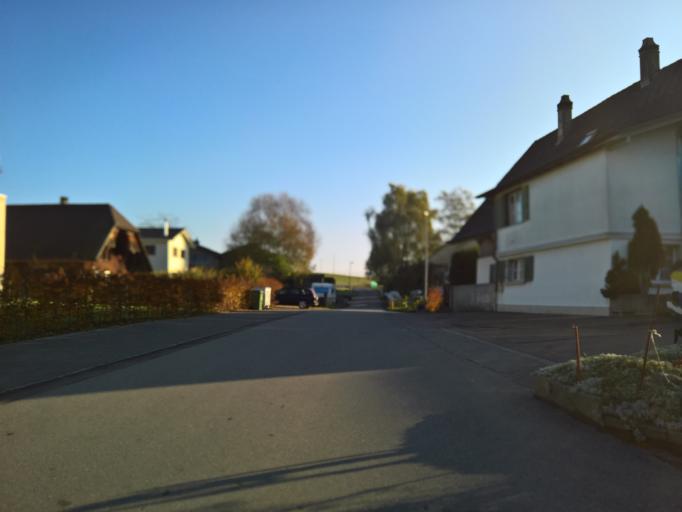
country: CH
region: Bern
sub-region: Bern-Mittelland District
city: Kirchlindach
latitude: 46.9971
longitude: 7.4323
